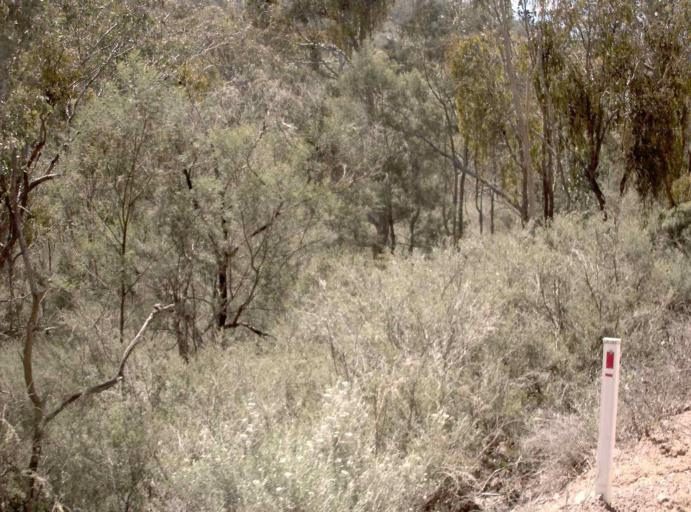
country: AU
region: New South Wales
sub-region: Snowy River
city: Jindabyne
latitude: -37.0397
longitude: 148.5386
